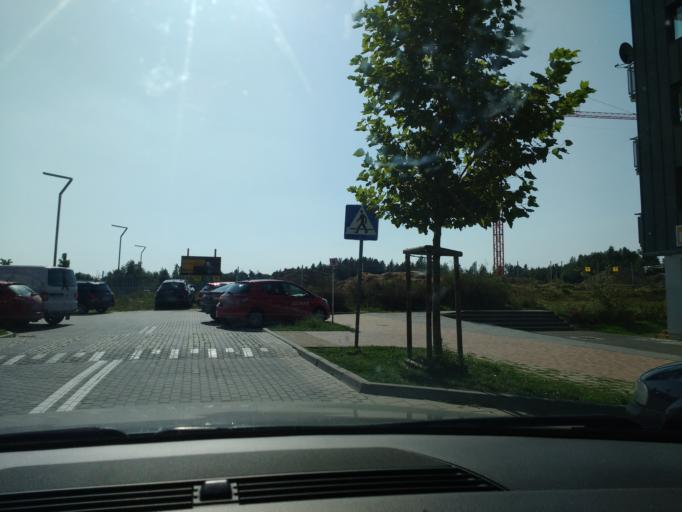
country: PL
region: Pomeranian Voivodeship
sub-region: Powiat kartuski
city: Chwaszczyno
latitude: 54.4857
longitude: 18.4277
